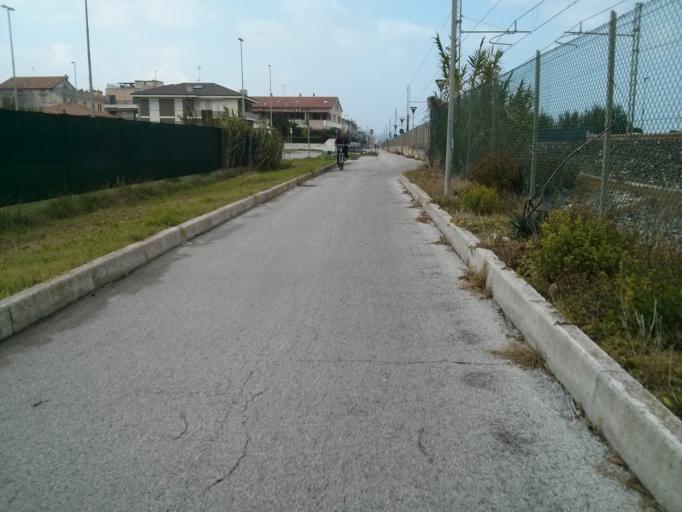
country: IT
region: The Marches
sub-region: Provincia di Pesaro e Urbino
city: Fano
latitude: 43.8574
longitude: 12.9992
